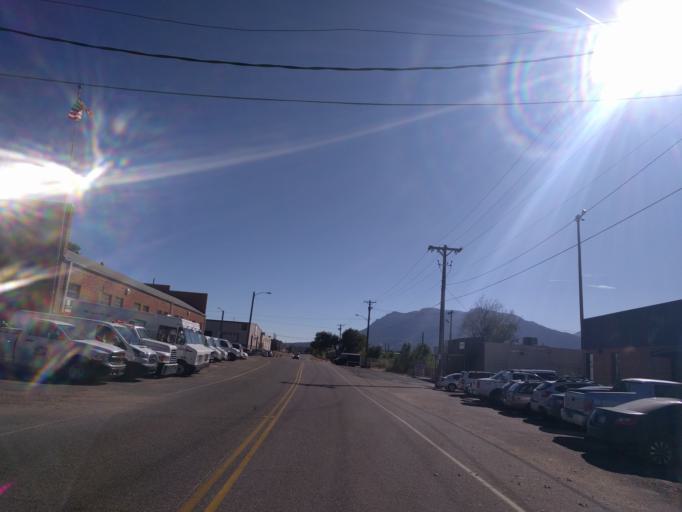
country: US
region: Colorado
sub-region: El Paso County
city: Colorado Springs
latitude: 38.8321
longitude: -104.8290
